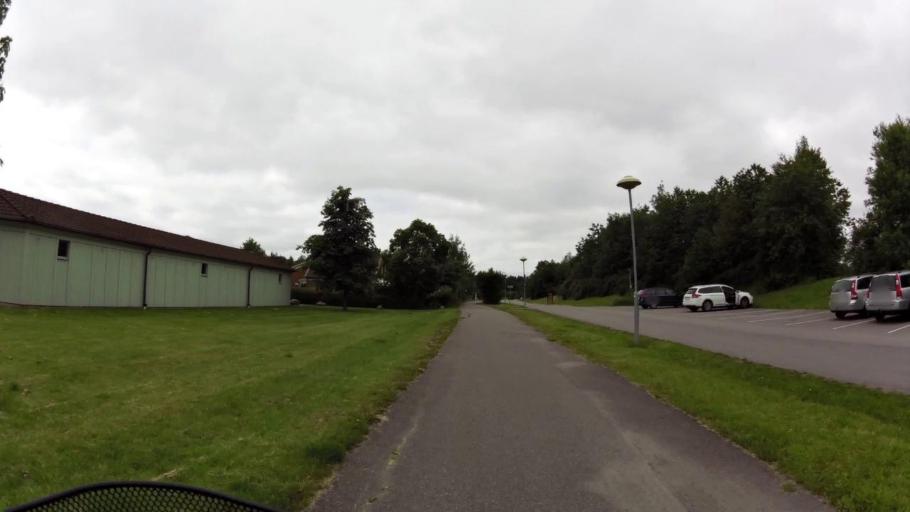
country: SE
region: OEstergoetland
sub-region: Linkopings Kommun
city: Sturefors
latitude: 58.3720
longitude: 15.6851
